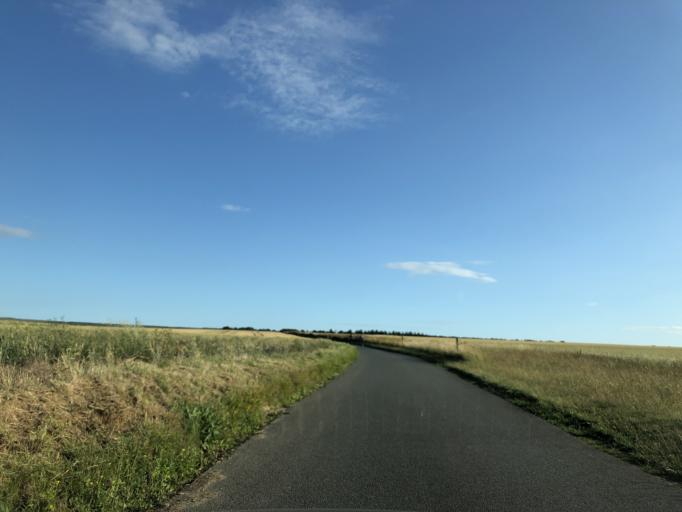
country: GB
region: England
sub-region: Isle of Wight
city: Yarmouth
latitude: 50.6951
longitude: -1.4719
